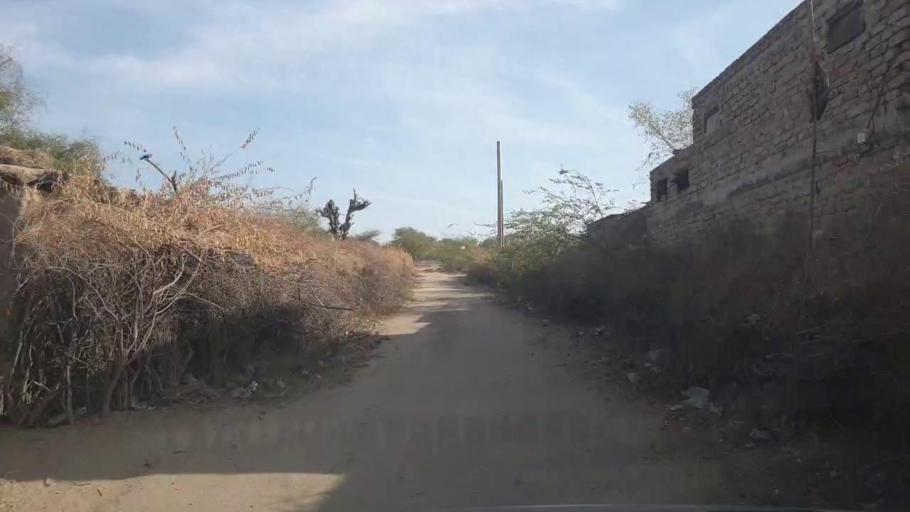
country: PK
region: Sindh
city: Nabisar
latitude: 25.0638
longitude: 69.6428
